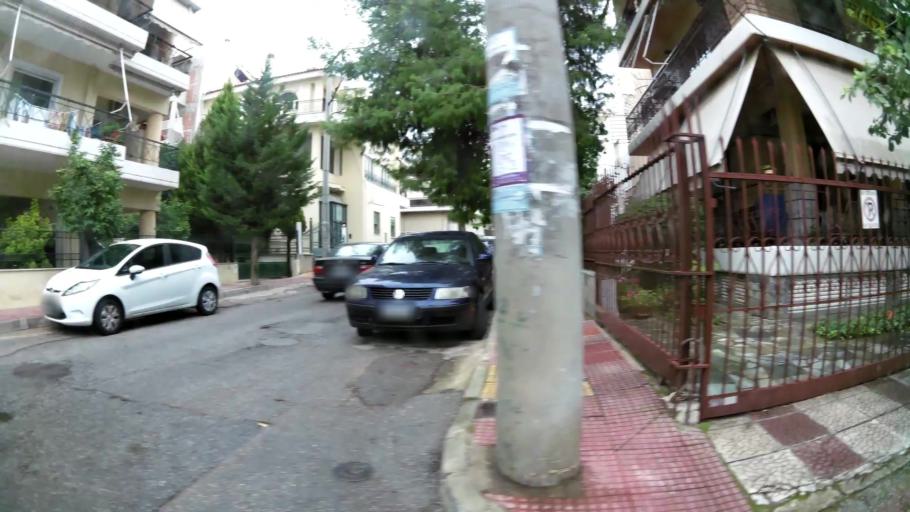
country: GR
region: Attica
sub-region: Nomarchia Athinas
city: Agioi Anargyroi
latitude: 38.0291
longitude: 23.7250
